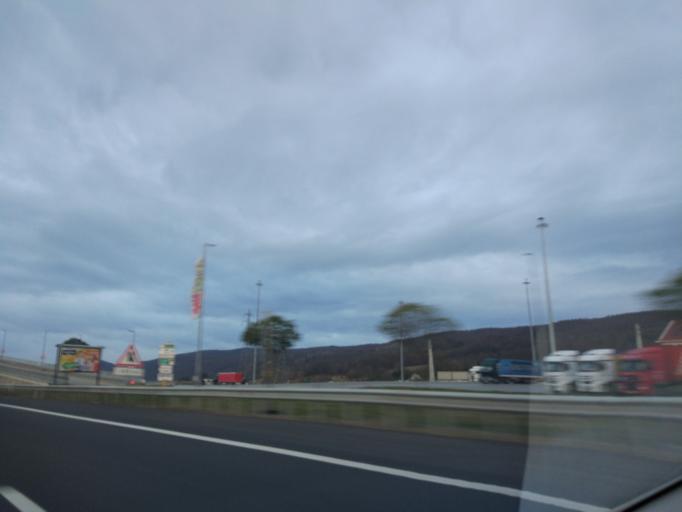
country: TR
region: Bolu
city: Bolu
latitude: 40.7247
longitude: 31.4645
